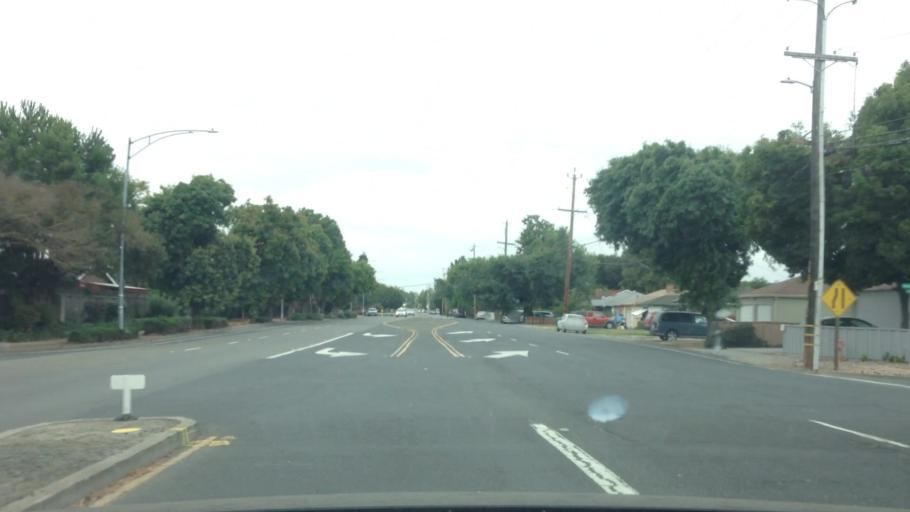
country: US
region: California
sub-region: Alameda County
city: Fremont
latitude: 37.5609
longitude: -121.9964
